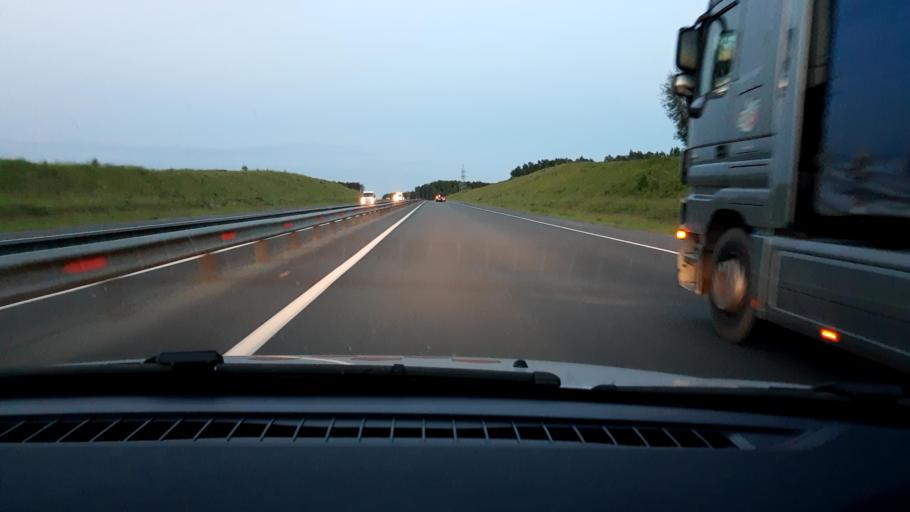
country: RU
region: Nizjnij Novgorod
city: Kstovo
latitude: 56.0735
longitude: 44.1082
